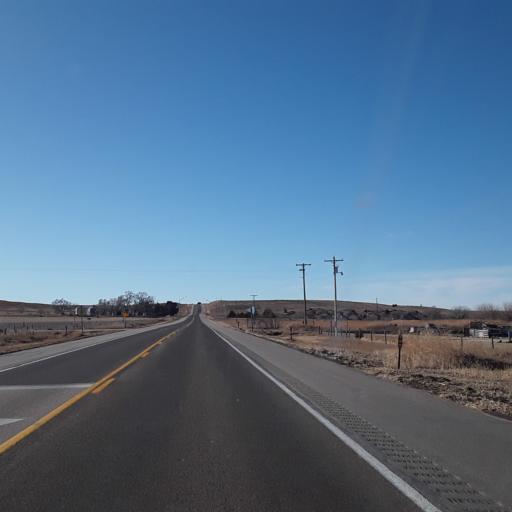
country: US
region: Nebraska
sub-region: Hitchcock County
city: Trenton
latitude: 40.2344
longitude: -100.8894
